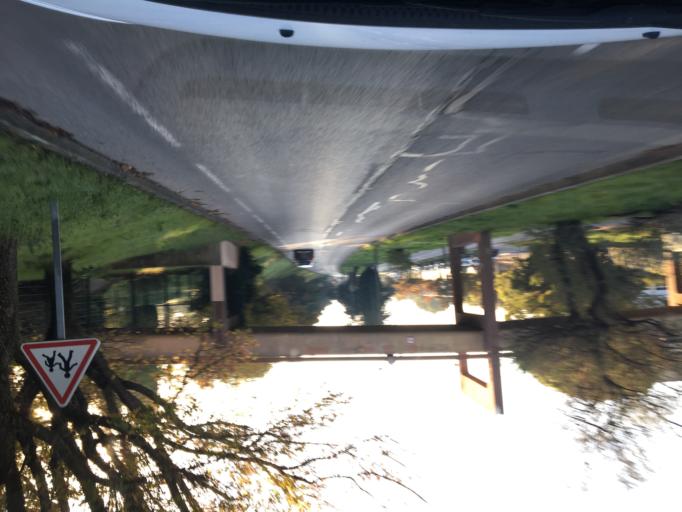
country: FR
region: Provence-Alpes-Cote d'Azur
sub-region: Departement des Bouches-du-Rhone
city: Aix-en-Provence
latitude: 43.5251
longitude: 5.4194
